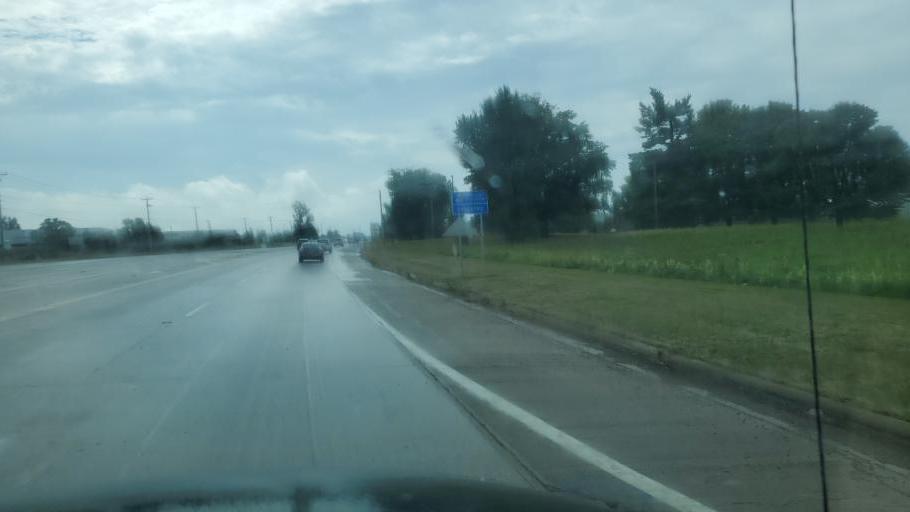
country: US
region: Ohio
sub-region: Licking County
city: Hebron
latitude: 39.9797
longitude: -82.4862
